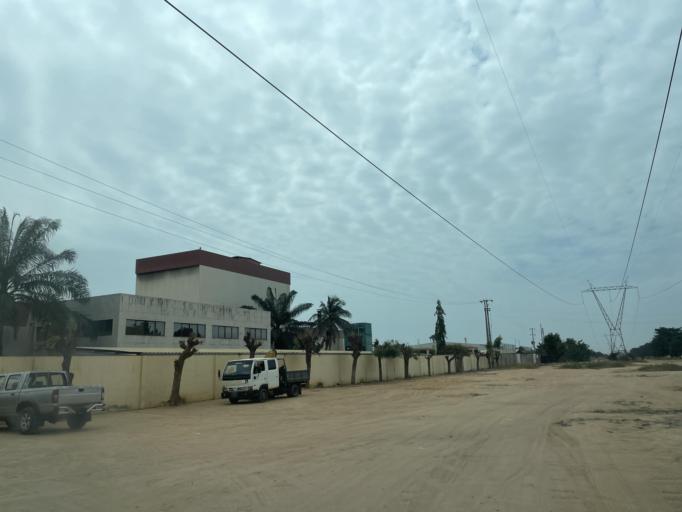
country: AO
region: Luanda
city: Luanda
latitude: -8.9259
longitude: 13.3918
